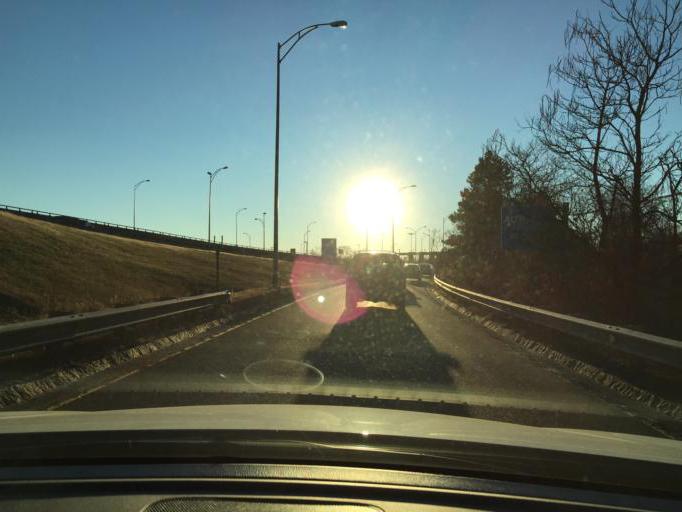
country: US
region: Massachusetts
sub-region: Middlesex County
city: Cambridge
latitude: 42.3587
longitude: -71.1218
